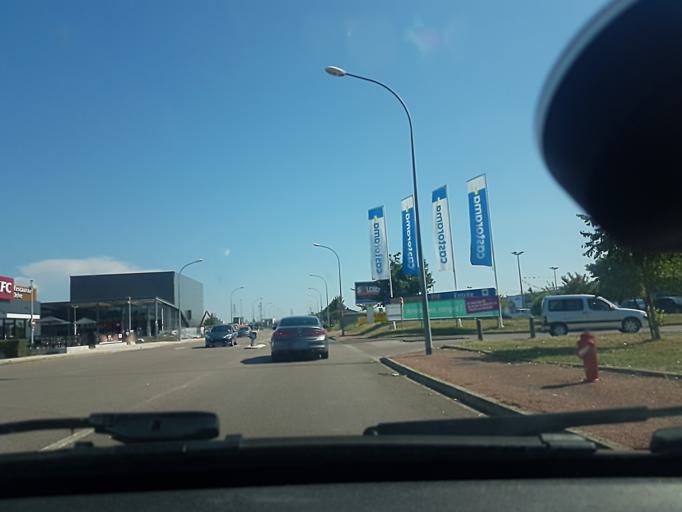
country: FR
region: Bourgogne
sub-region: Departement de Saone-et-Loire
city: Chalon-sur-Saone
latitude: 46.7757
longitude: 4.8643
